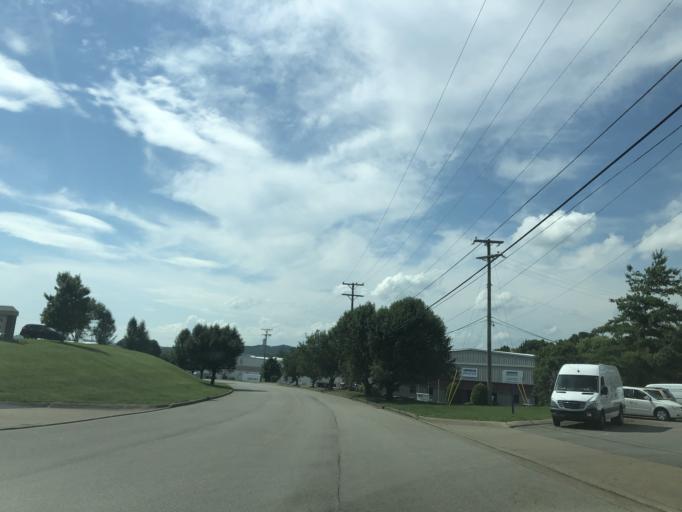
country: US
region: Tennessee
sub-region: Davidson County
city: Nashville
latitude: 36.2264
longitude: -86.7869
